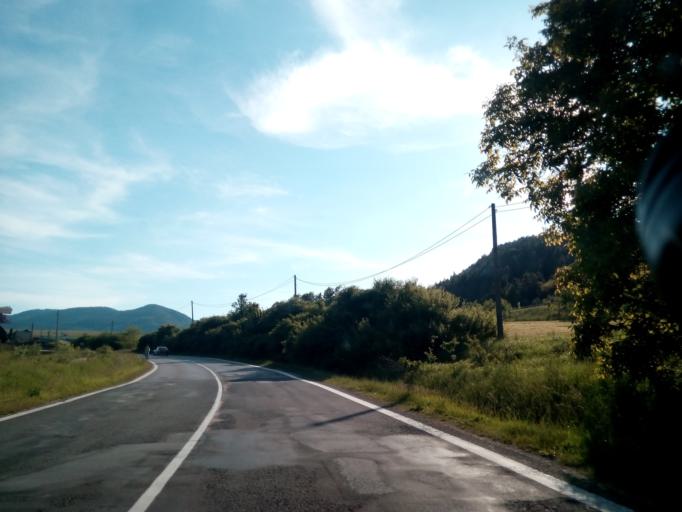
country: SK
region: Kosicky
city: Krompachy
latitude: 49.0138
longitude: 20.9473
